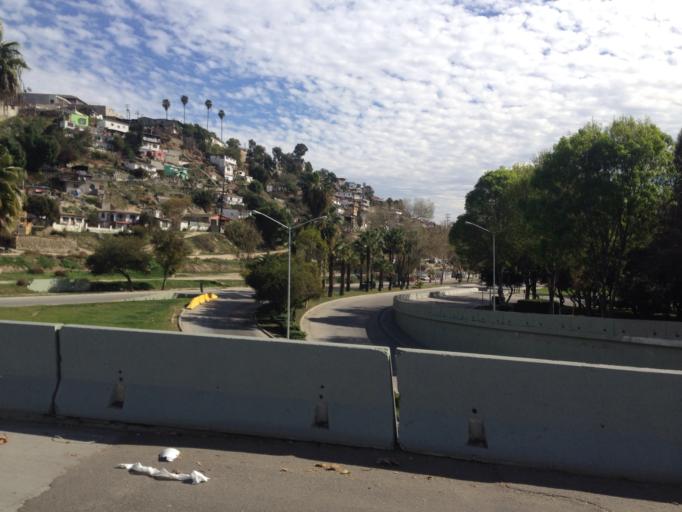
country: MX
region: Baja California
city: Tijuana
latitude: 32.5240
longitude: -117.0070
